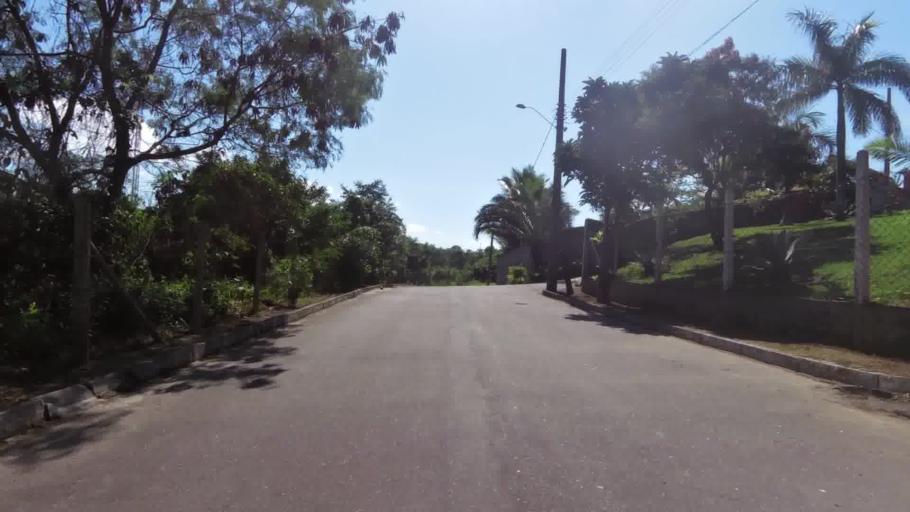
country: BR
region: Espirito Santo
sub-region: Piuma
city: Piuma
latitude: -20.8036
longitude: -40.6014
